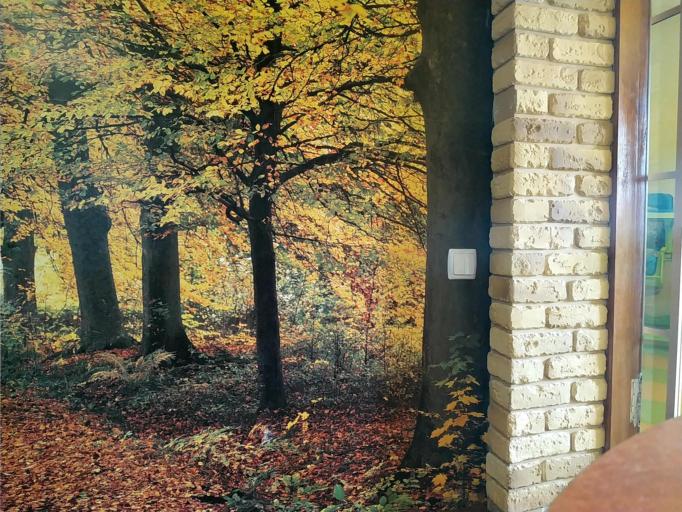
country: RU
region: Smolensk
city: Katyn'
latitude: 54.9207
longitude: 31.7562
